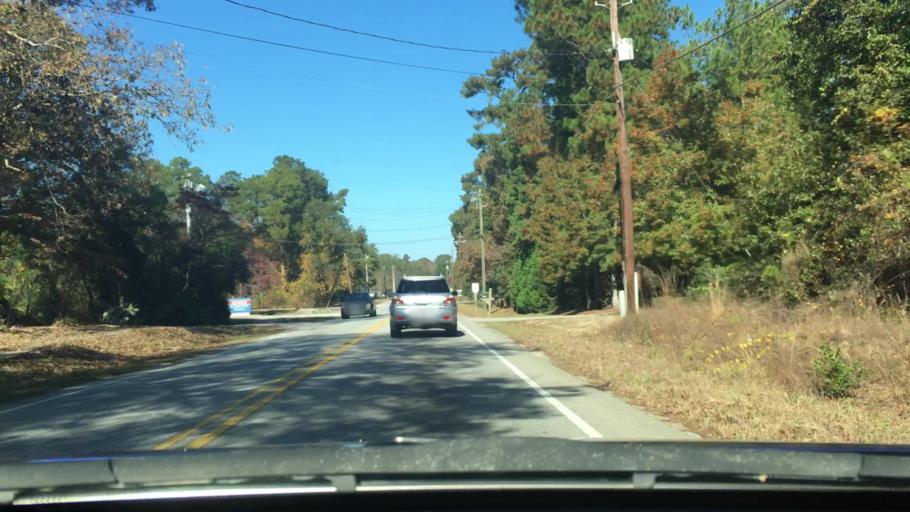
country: US
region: South Carolina
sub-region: Sumter County
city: South Sumter
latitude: 33.8903
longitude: -80.3663
